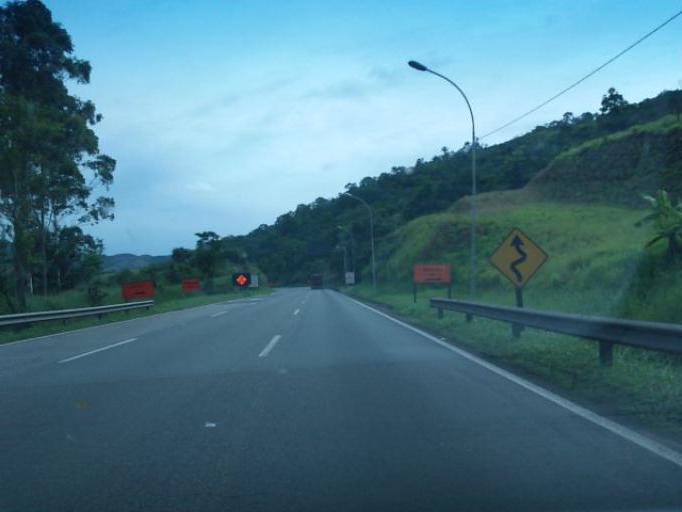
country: BR
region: Sao Paulo
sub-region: Cajati
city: Cajati
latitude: -24.8172
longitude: -48.2140
